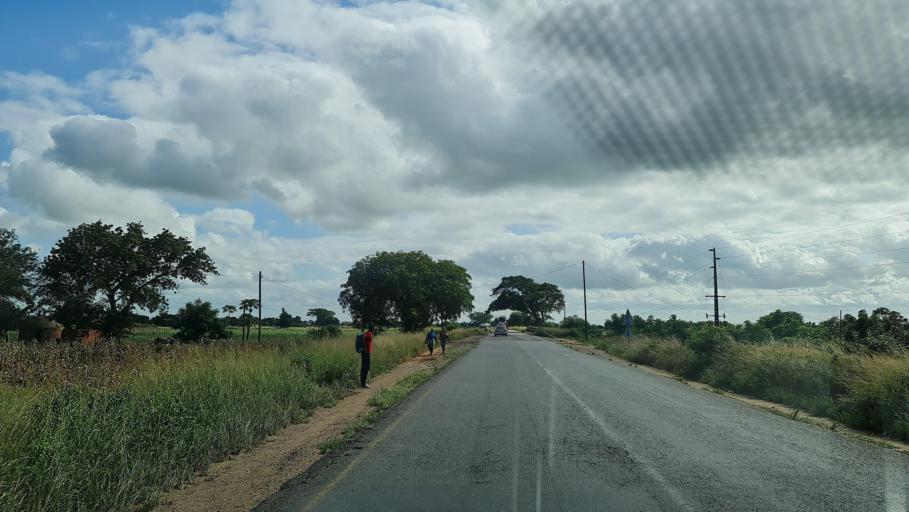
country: MZ
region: Gaza
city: Macia
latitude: -25.0868
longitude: 32.8445
